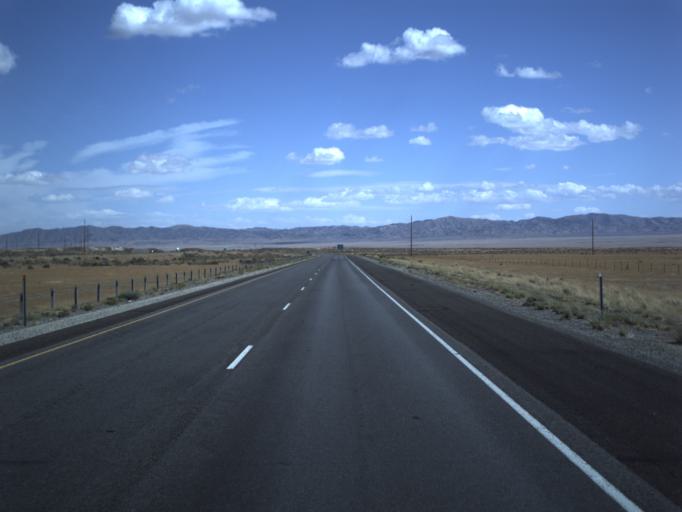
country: US
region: Utah
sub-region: Tooele County
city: Grantsville
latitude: 40.7251
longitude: -113.1490
